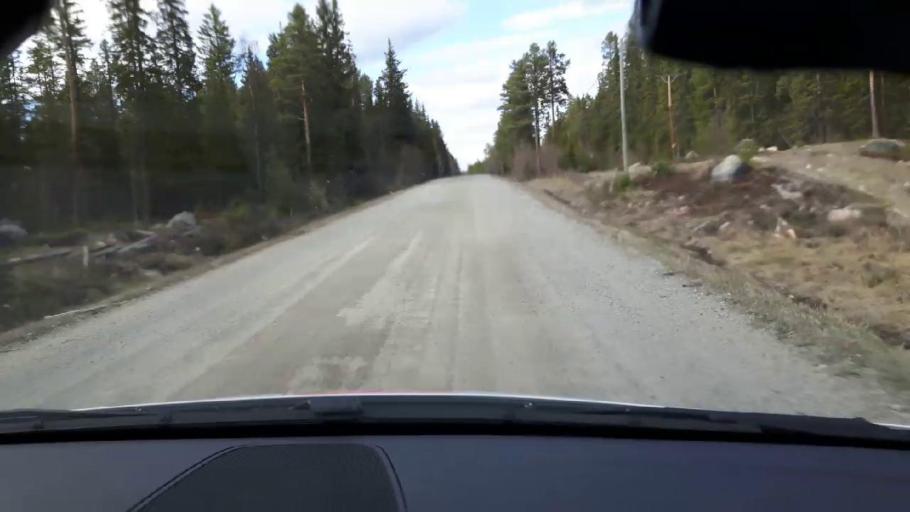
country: SE
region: Jaemtland
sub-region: Bergs Kommun
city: Hoverberg
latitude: 62.6691
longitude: 14.7461
